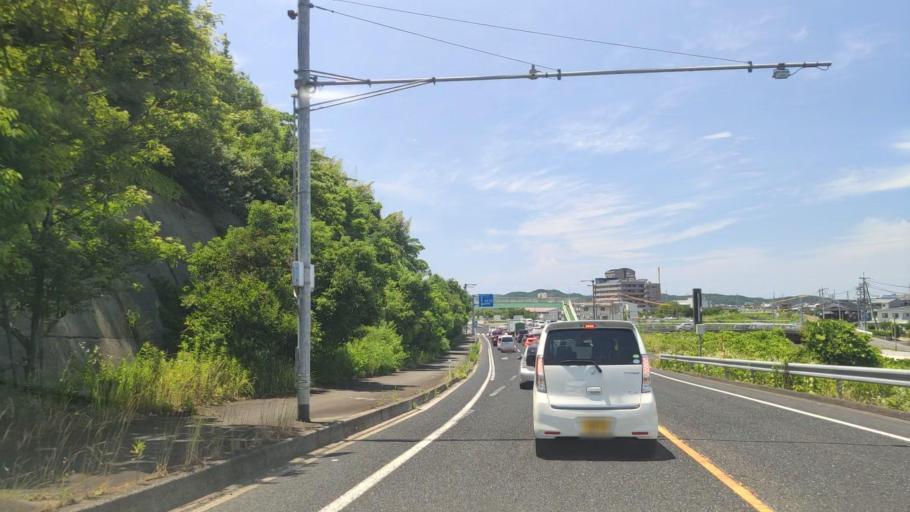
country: JP
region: Tottori
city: Tottori
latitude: 35.4723
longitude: 134.2398
